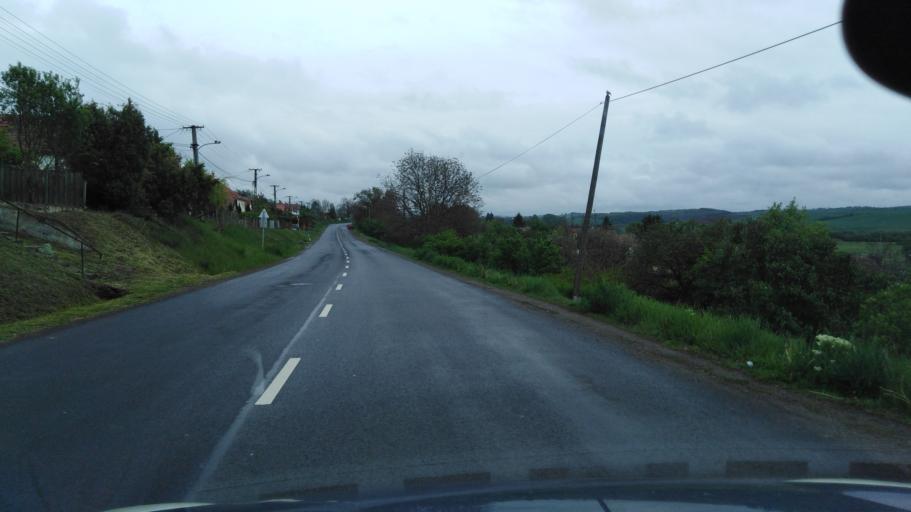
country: HU
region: Nograd
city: Karancskeszi
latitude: 48.1225
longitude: 19.6390
